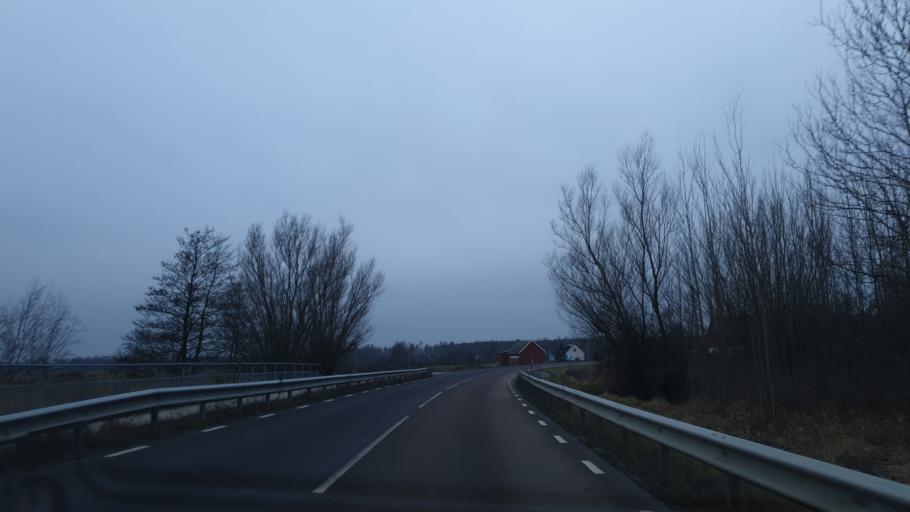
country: SE
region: Blekinge
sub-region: Karlskrona Kommun
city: Jaemjoe
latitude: 56.1731
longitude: 15.7265
